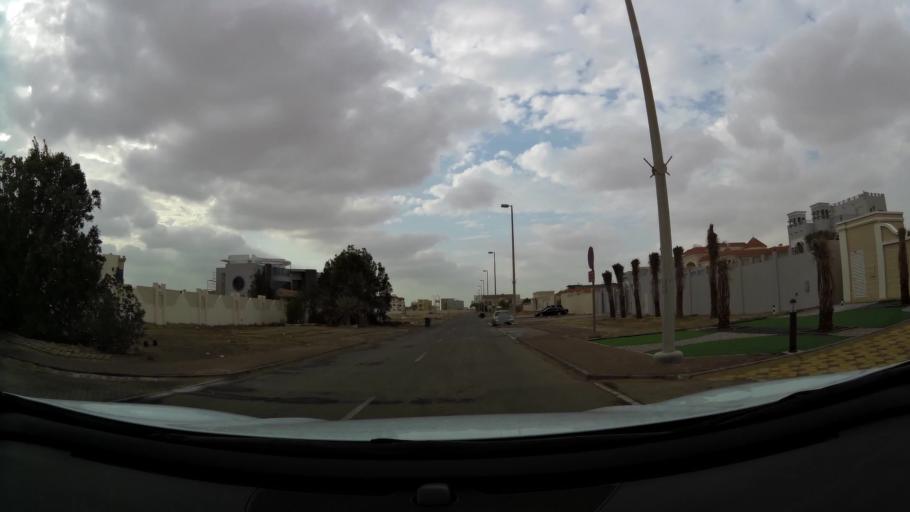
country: AE
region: Abu Dhabi
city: Abu Dhabi
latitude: 24.3506
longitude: 54.6182
